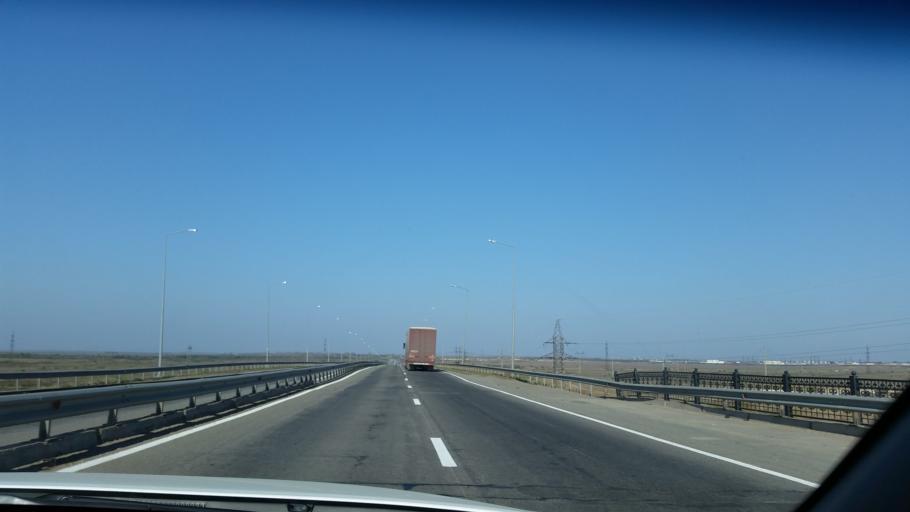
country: KZ
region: Astana Qalasy
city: Astana
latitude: 51.2285
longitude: 71.3262
